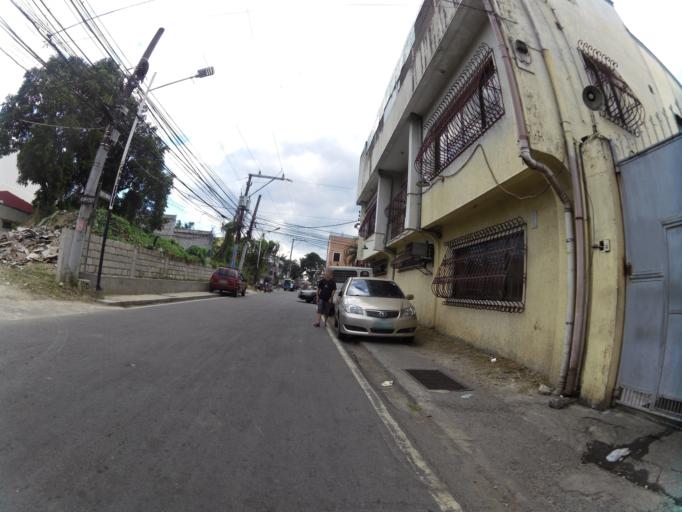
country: PH
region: Calabarzon
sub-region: Province of Rizal
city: Antipolo
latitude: 14.6307
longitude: 121.1082
